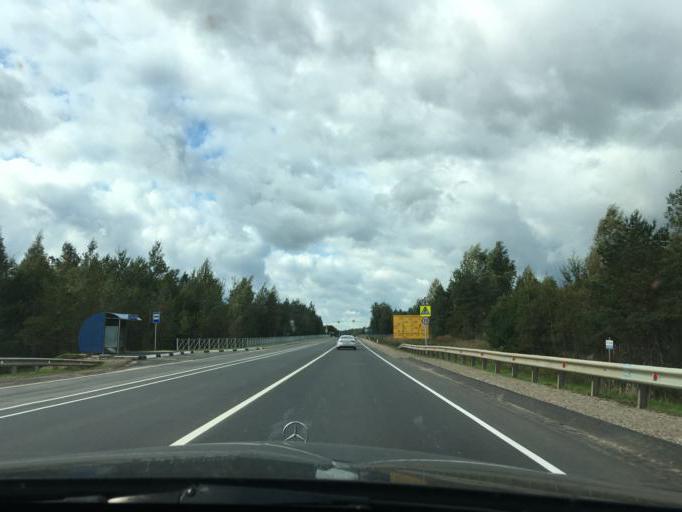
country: RU
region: Tverskaya
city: Toropets
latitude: 56.3279
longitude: 31.2133
